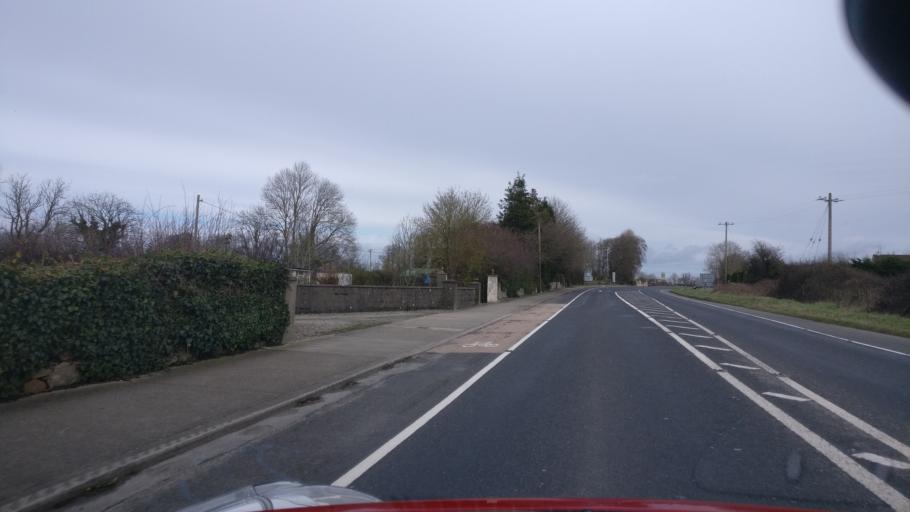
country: IE
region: Munster
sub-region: North Tipperary
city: Nenagh
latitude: 52.8565
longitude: -8.2324
